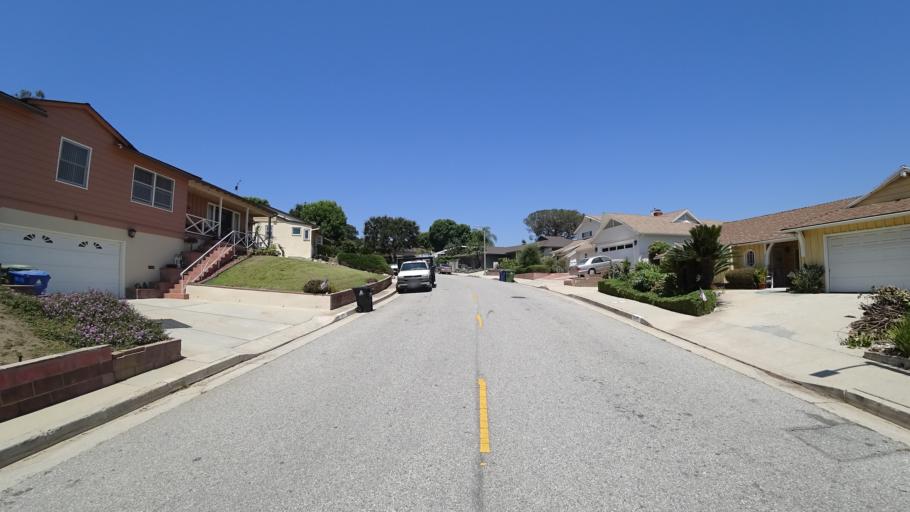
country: US
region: California
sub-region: Los Angeles County
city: View Park-Windsor Hills
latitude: 34.0137
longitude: -118.3592
